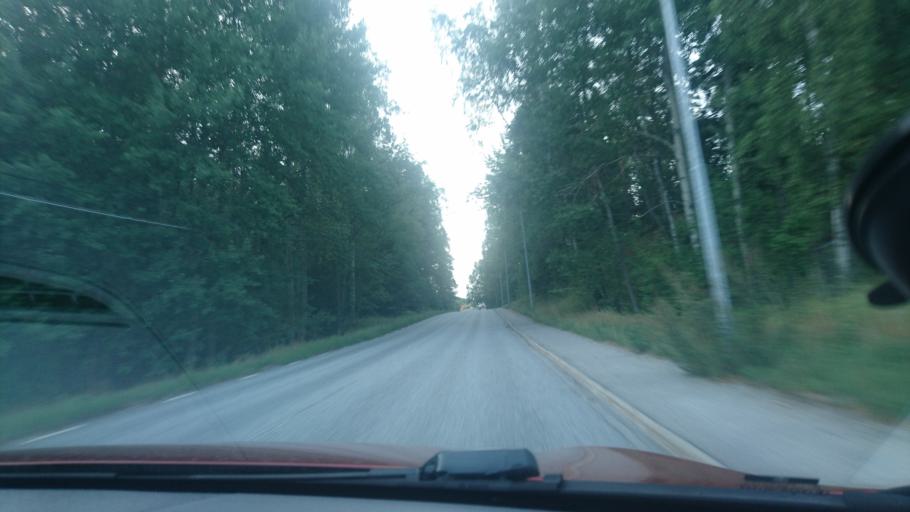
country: SE
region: Stockholm
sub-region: Sodertalje Kommun
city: Pershagen
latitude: 59.1517
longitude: 17.6508
